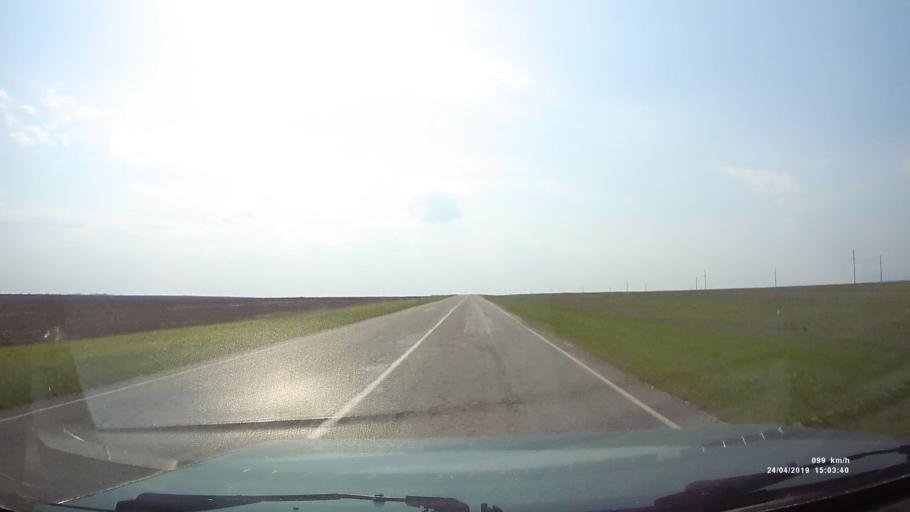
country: RU
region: Rostov
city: Remontnoye
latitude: 46.5643
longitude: 43.4871
